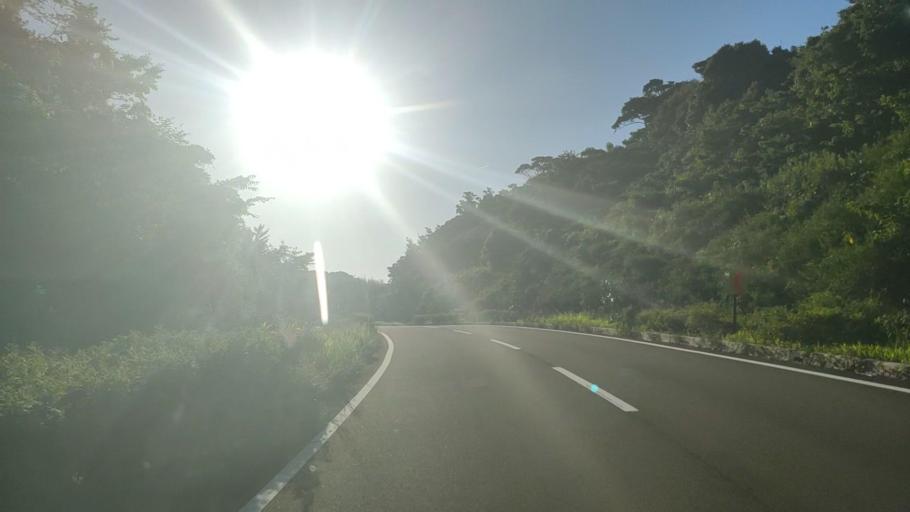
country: JP
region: Mie
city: Toba
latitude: 34.2765
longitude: 136.7713
